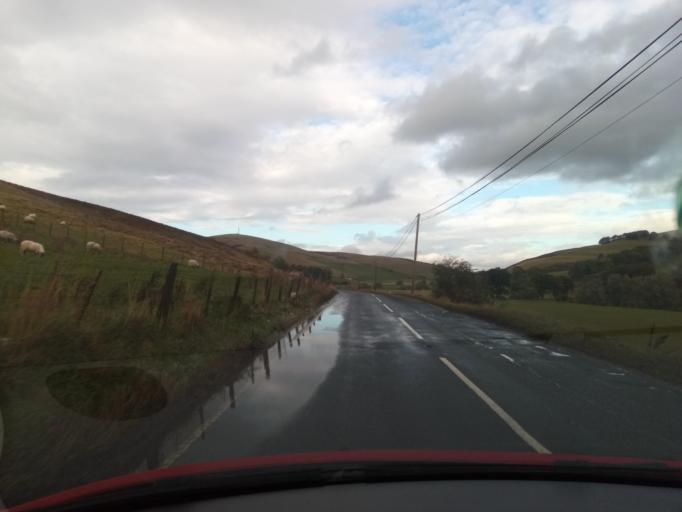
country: GB
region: Scotland
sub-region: The Scottish Borders
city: West Linton
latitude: 55.6696
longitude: -3.3224
